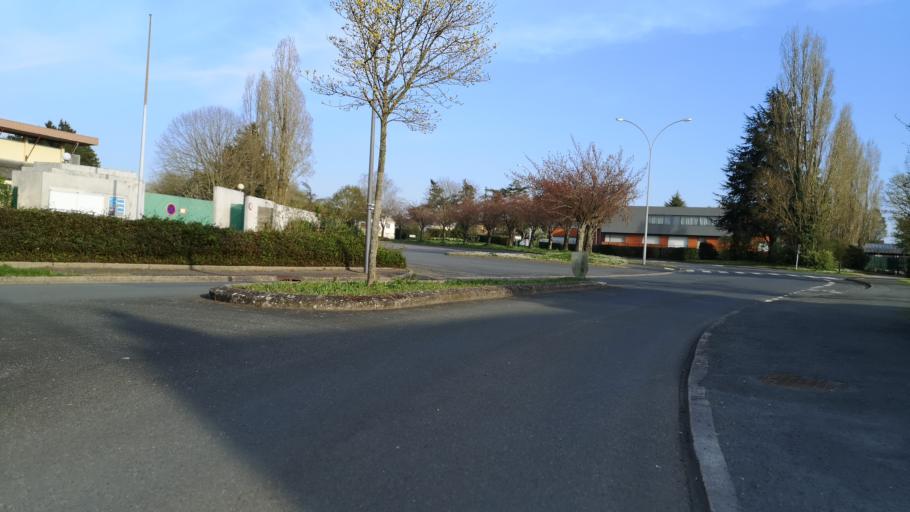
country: FR
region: Pays de la Loire
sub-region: Departement de Maine-et-Loire
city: Chemille-Melay
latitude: 47.2147
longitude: -0.7263
